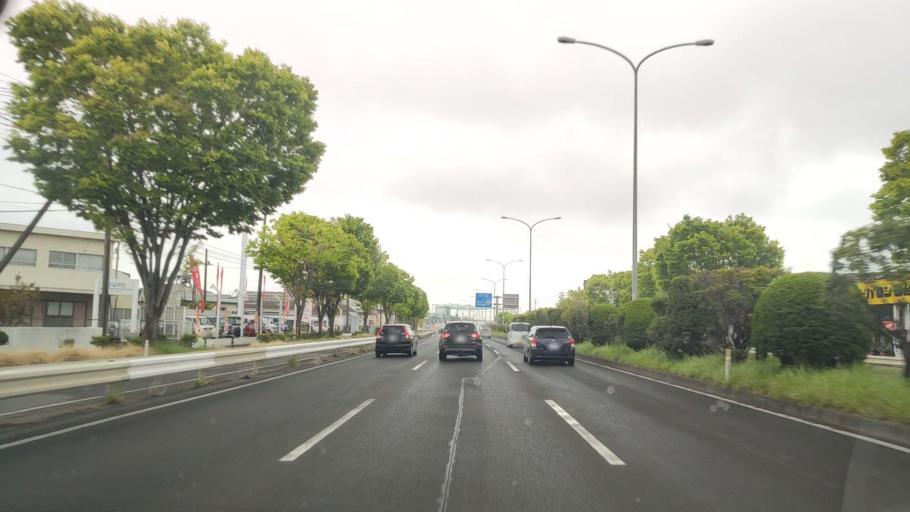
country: JP
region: Miyagi
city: Sendai-shi
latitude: 38.2411
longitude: 140.9193
